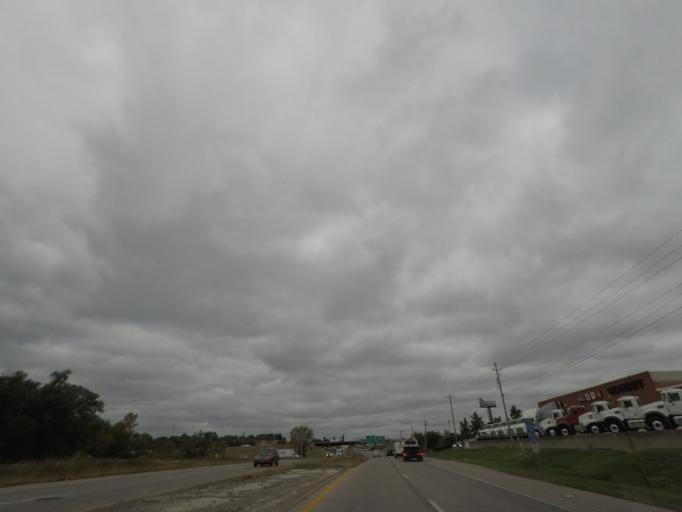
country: US
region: Iowa
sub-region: Polk County
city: Saylorville
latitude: 41.6462
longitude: -93.6005
